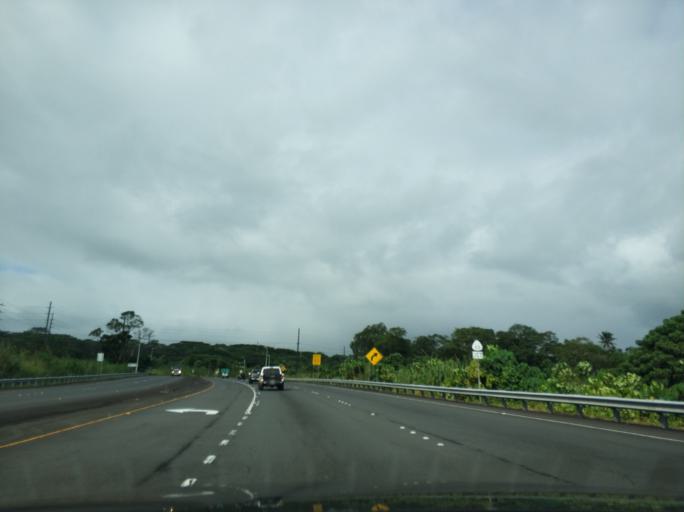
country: US
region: Hawaii
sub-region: Hawaii County
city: Kea'au
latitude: 19.6327
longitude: -155.0375
